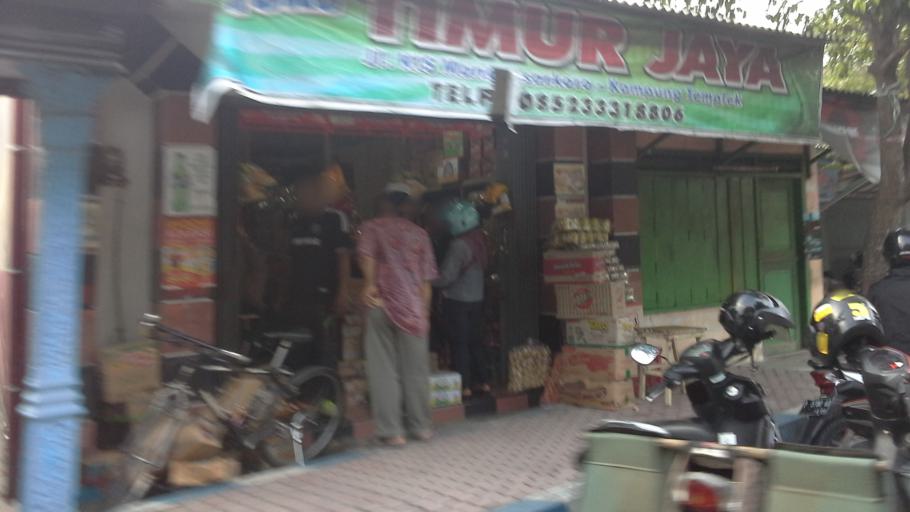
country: ID
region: East Java
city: Bondowoso
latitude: -7.9178
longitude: 113.8283
